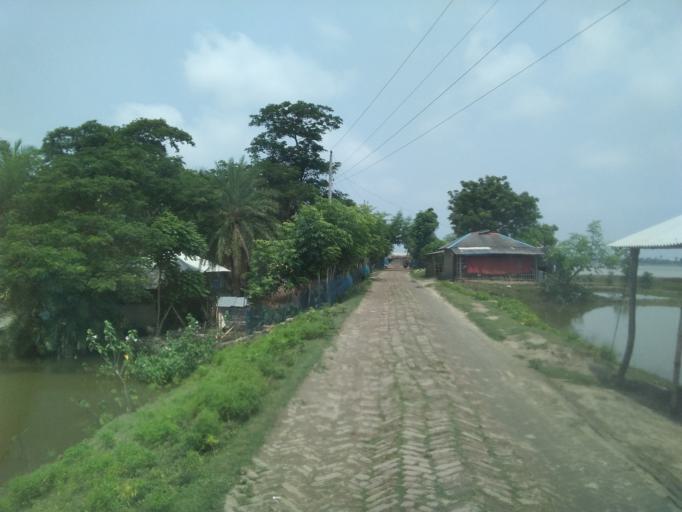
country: BD
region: Khulna
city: Phultala
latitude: 22.6413
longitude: 89.4270
